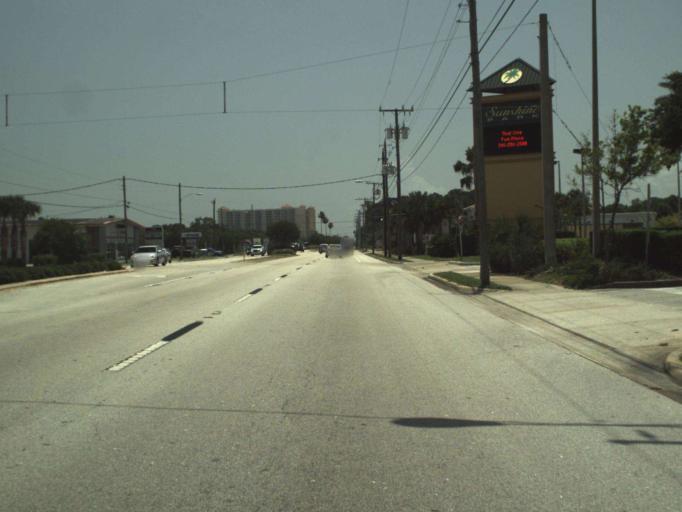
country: US
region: Florida
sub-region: Volusia County
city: South Daytona
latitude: 29.1671
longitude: -80.9996
